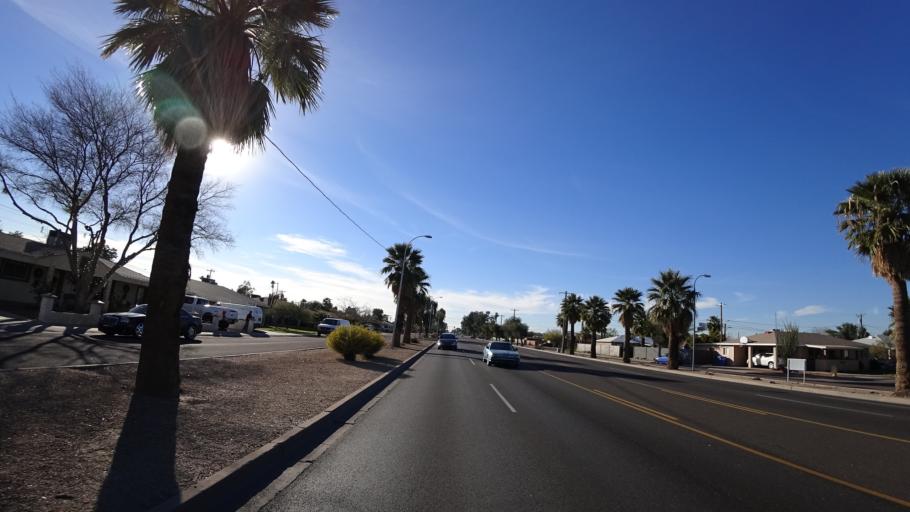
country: US
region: Arizona
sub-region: Maricopa County
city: Glendale
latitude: 33.5240
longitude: -112.1273
